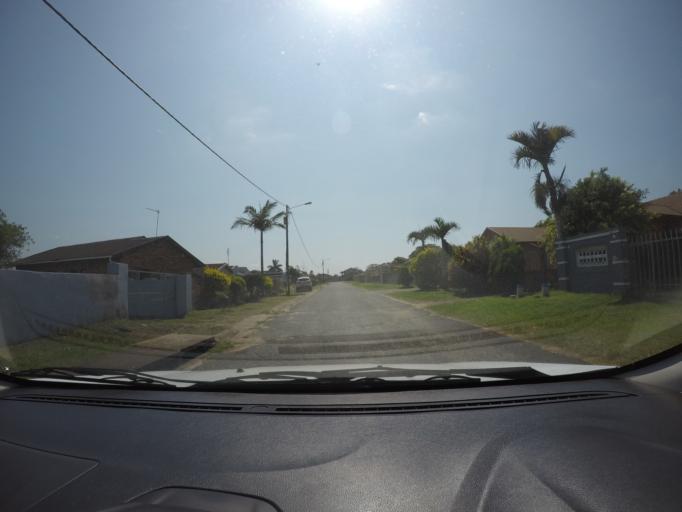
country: ZA
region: KwaZulu-Natal
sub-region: uThungulu District Municipality
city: eSikhawini
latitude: -28.8680
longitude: 31.9151
